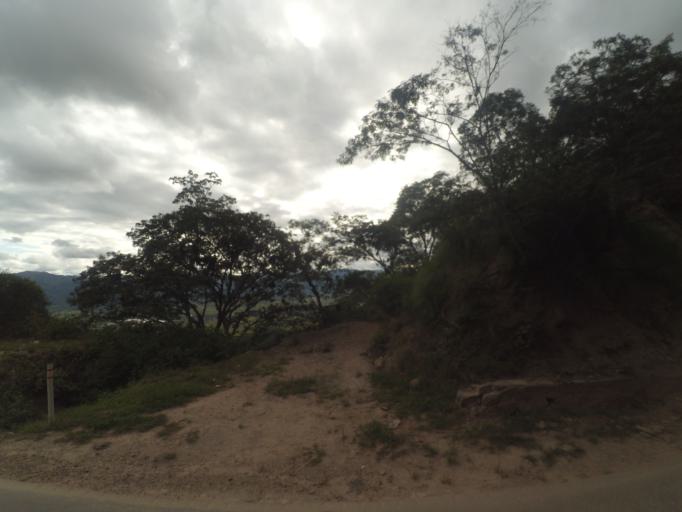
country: BO
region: Santa Cruz
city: Samaipata
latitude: -18.1704
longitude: -63.8875
